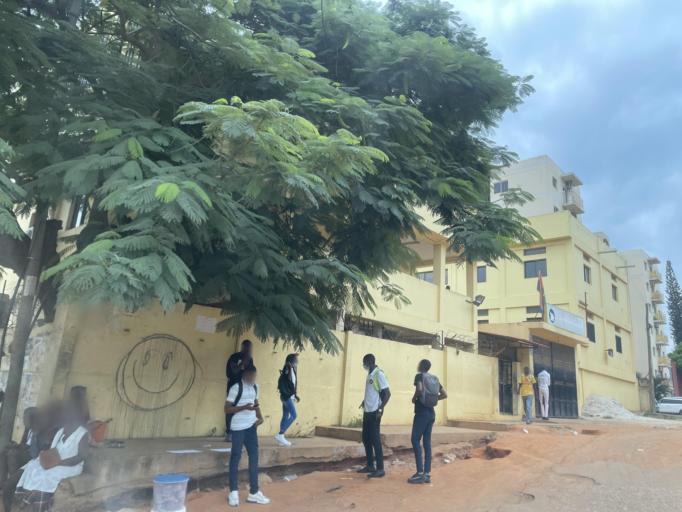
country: AO
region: Luanda
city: Luanda
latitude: -8.9120
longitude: 13.3760
